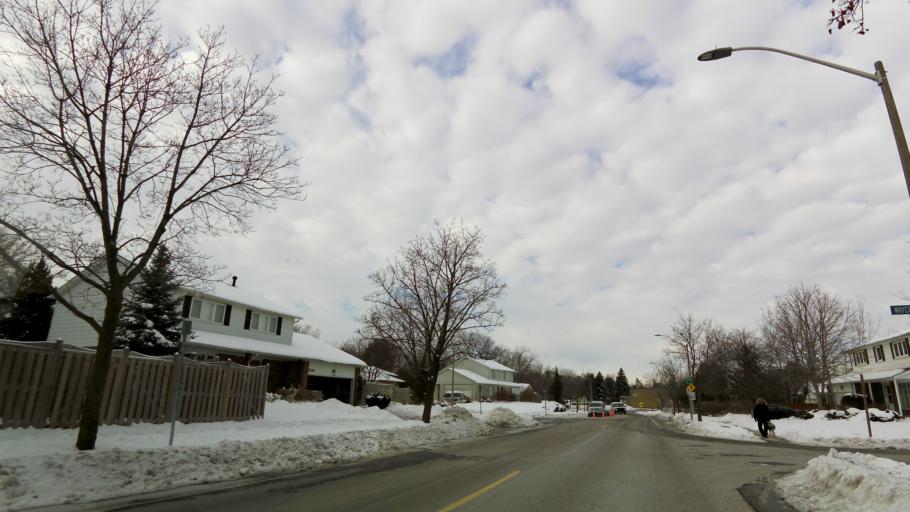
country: CA
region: Ontario
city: Mississauga
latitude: 43.5283
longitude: -79.6647
